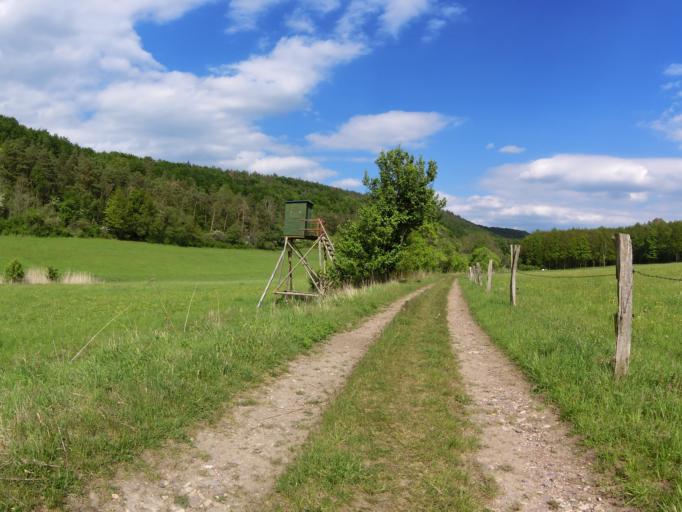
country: DE
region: Thuringia
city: Seebach
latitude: 50.9617
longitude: 10.4256
